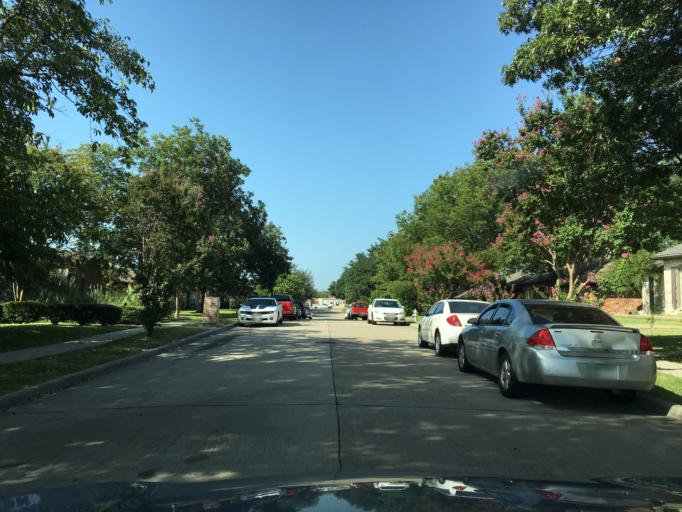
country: US
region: Texas
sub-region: Dallas County
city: Garland
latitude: 32.8739
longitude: -96.6127
